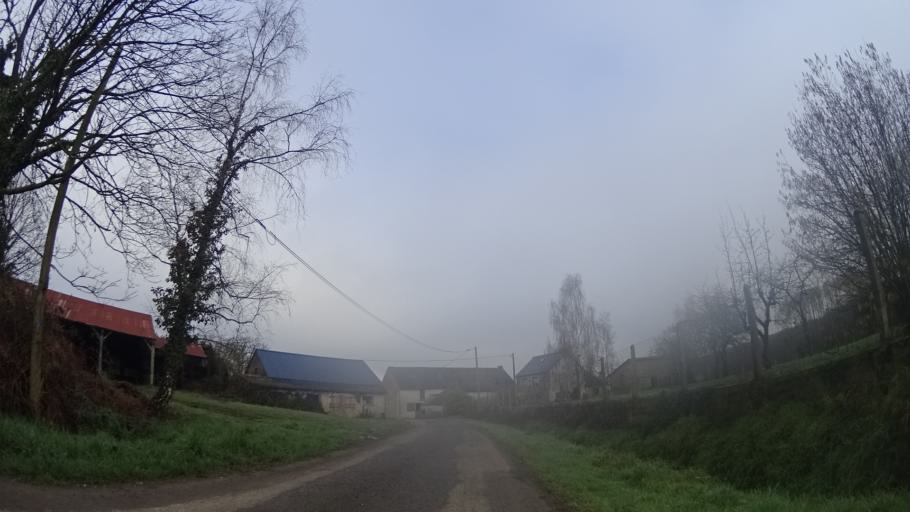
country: FR
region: Brittany
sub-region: Departement d'Ille-et-Vilaine
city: Saint-Domineuc
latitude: 48.3411
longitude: -1.9286
